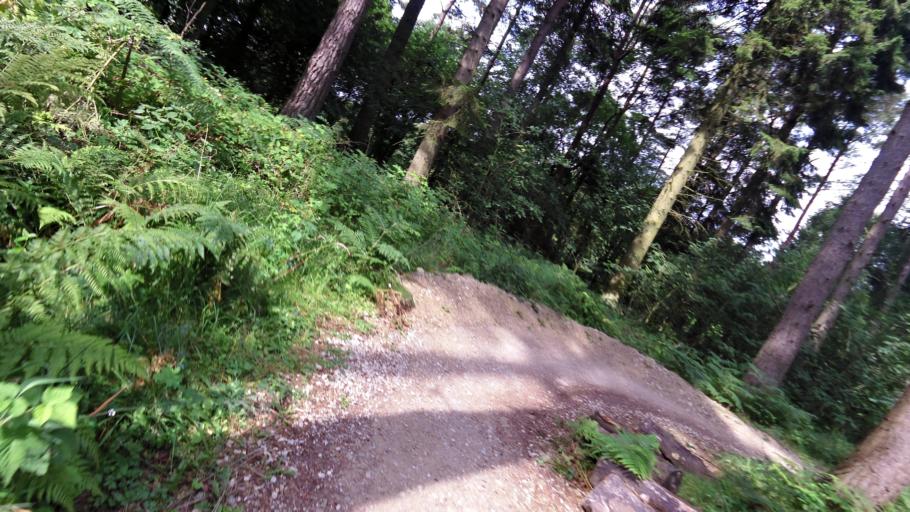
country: GB
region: England
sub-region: North Yorkshire
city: Thornton Dale
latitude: 54.2965
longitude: -0.6413
